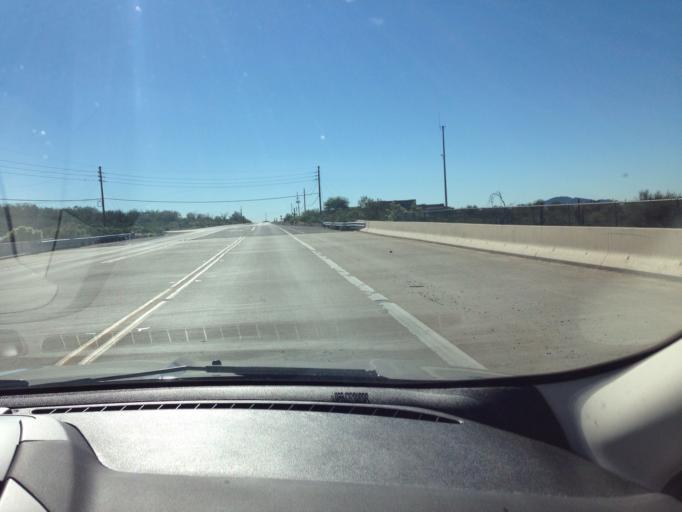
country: US
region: Arizona
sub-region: Maricopa County
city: New River
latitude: 33.8860
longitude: -112.0727
